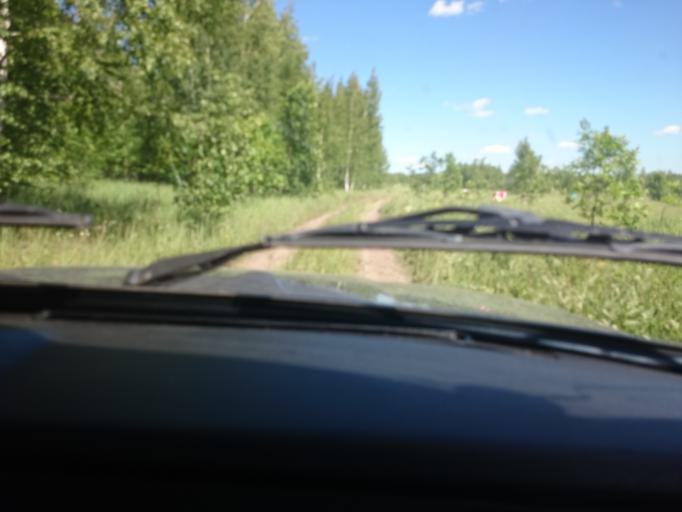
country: RU
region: Mordoviya
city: Kadoshkino
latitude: 54.0523
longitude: 44.4830
